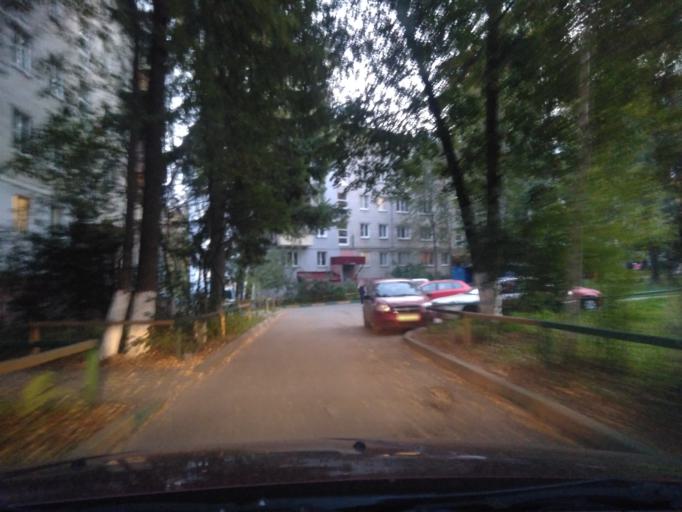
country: RU
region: Nizjnij Novgorod
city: Nizhniy Novgorod
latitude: 56.2908
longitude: 44.0451
